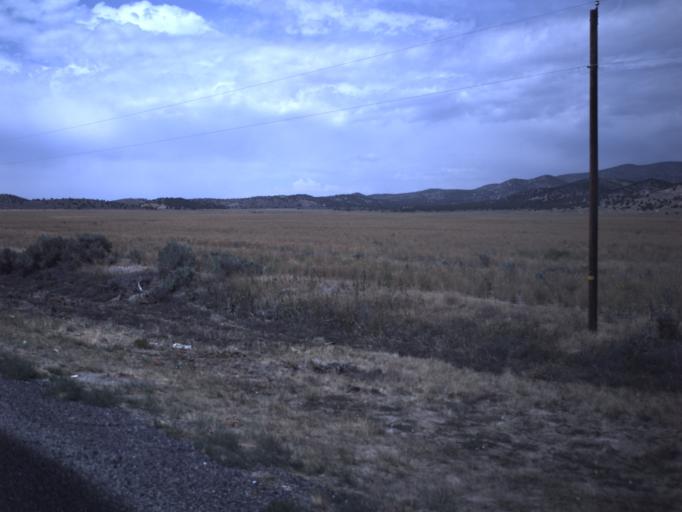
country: US
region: Utah
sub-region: Utah County
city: Eagle Mountain
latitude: 40.2493
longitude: -112.1244
